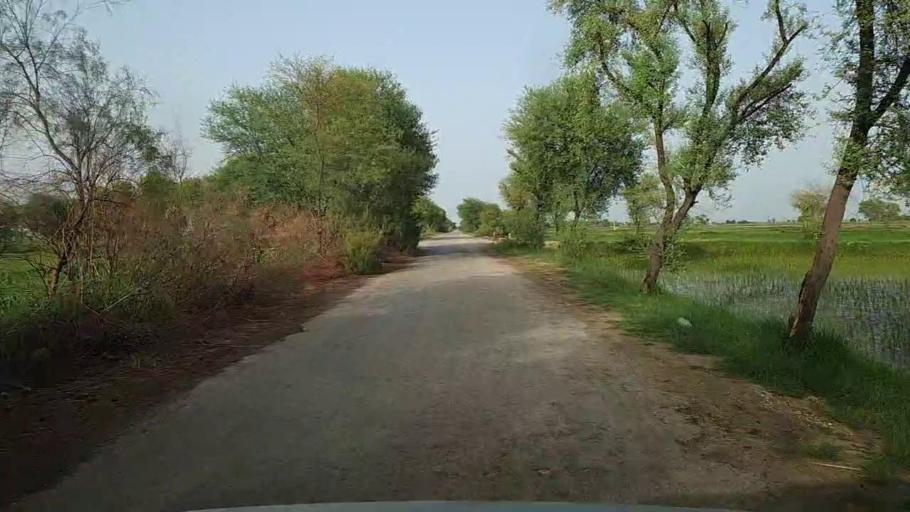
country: PK
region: Sindh
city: Khairpur Nathan Shah
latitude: 27.1561
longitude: 67.7431
